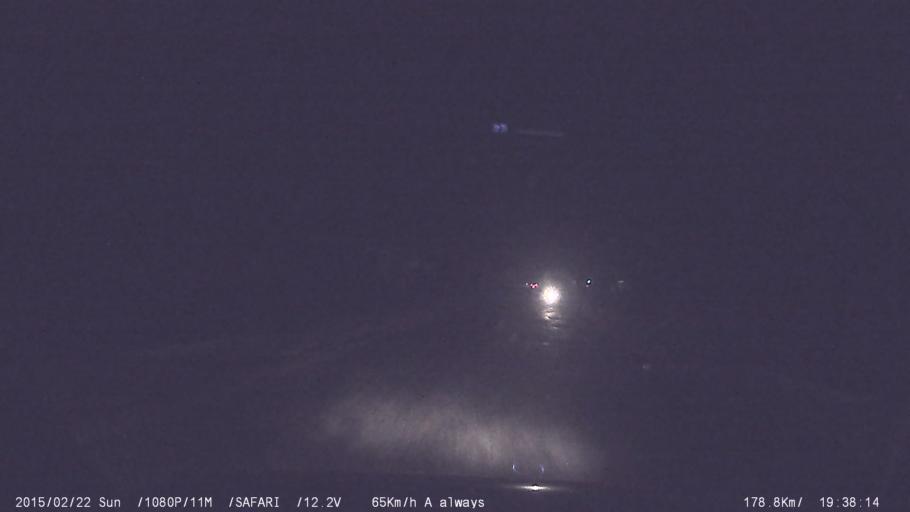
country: IN
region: Tamil Nadu
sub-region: Theni
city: Devadanappatti
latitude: 10.1420
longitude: 77.6294
